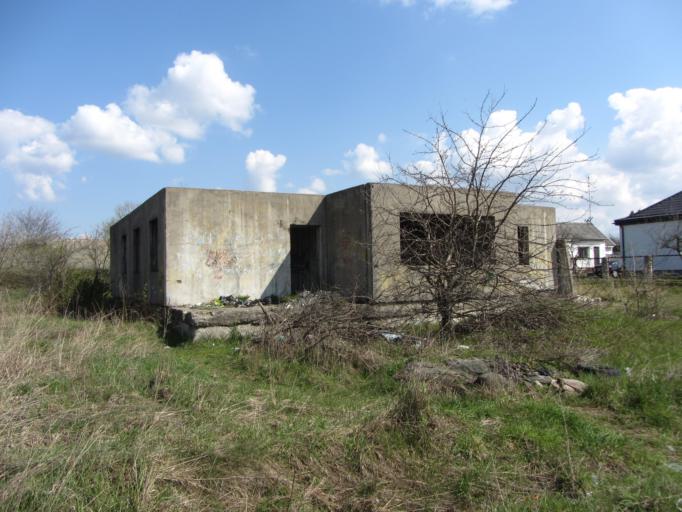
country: LT
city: Lentvaris
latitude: 54.6384
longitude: 25.0384
